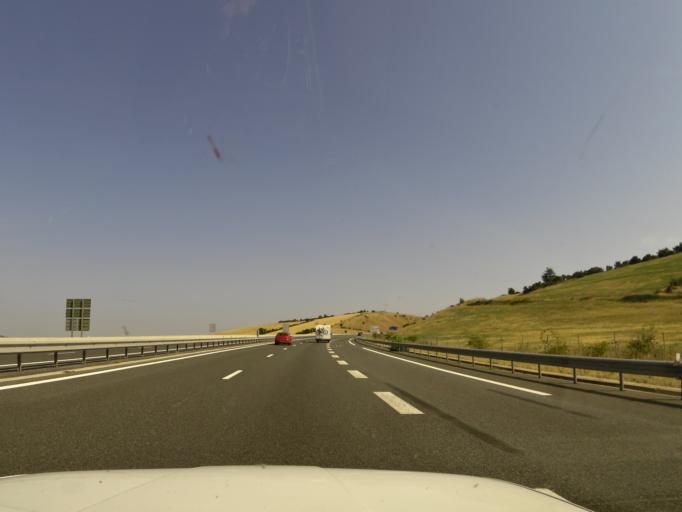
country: FR
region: Midi-Pyrenees
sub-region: Departement de l'Aveyron
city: Creissels
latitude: 44.1319
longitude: 3.0284
